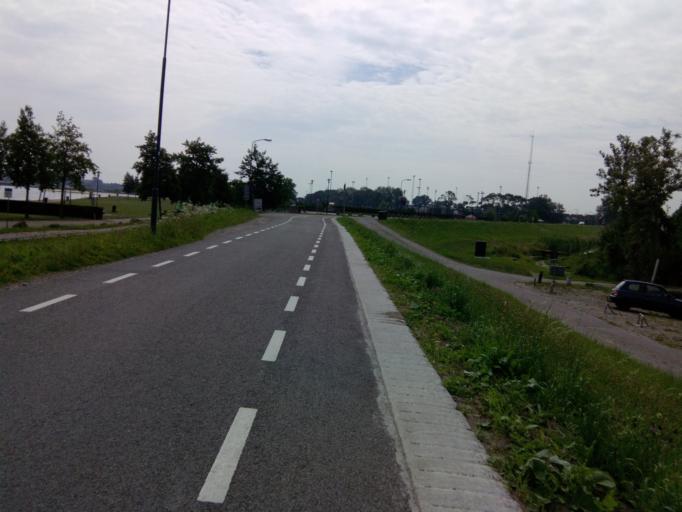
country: NL
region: Utrecht
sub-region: Gemeente Bunschoten
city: Spakenburg
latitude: 52.2601
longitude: 5.3727
